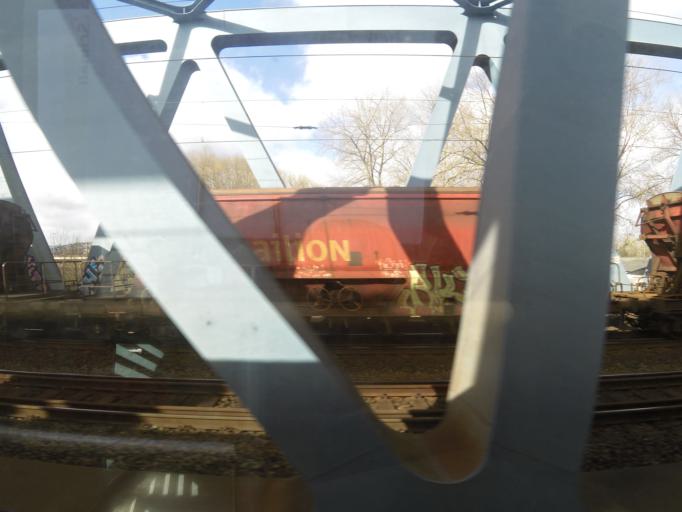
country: DE
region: Hamburg
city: Harburg
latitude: 53.4747
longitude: 9.9991
